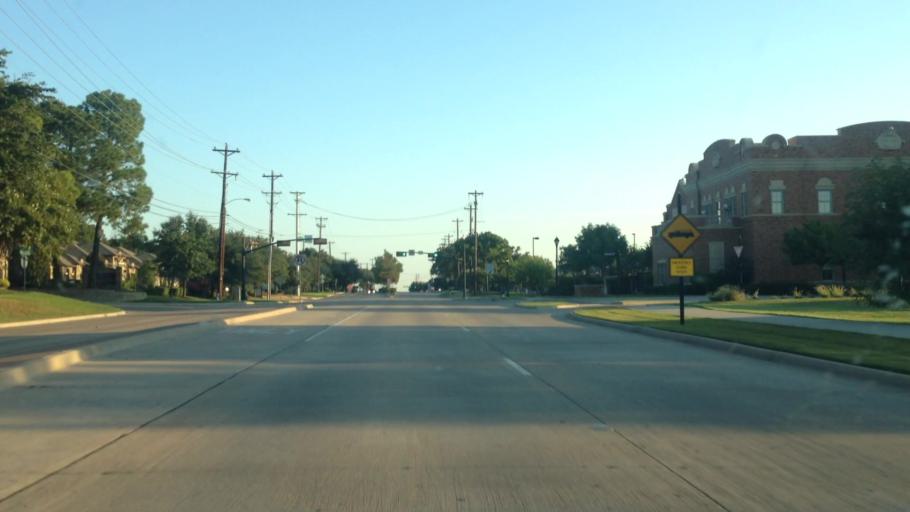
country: US
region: Texas
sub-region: Tarrant County
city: Southlake
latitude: 32.9469
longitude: -97.1341
